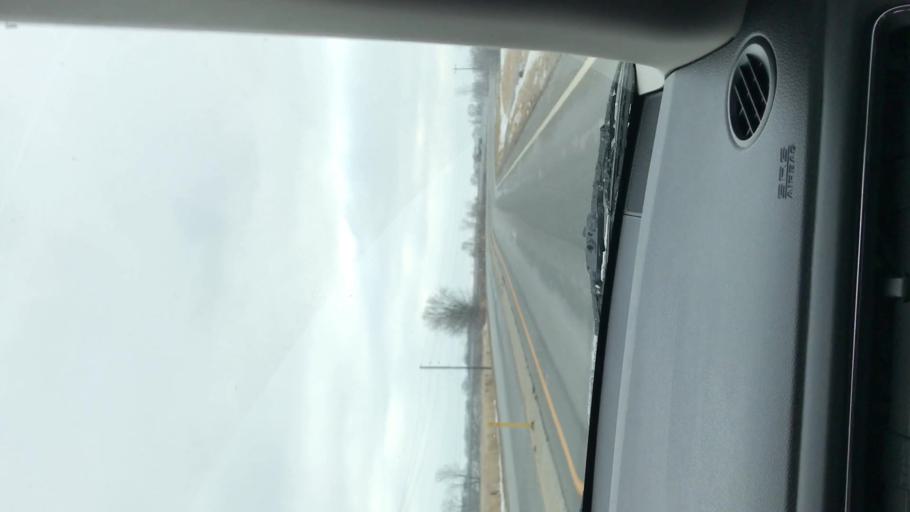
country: US
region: Ohio
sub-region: Hancock County
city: Findlay
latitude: 40.9946
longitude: -83.6480
